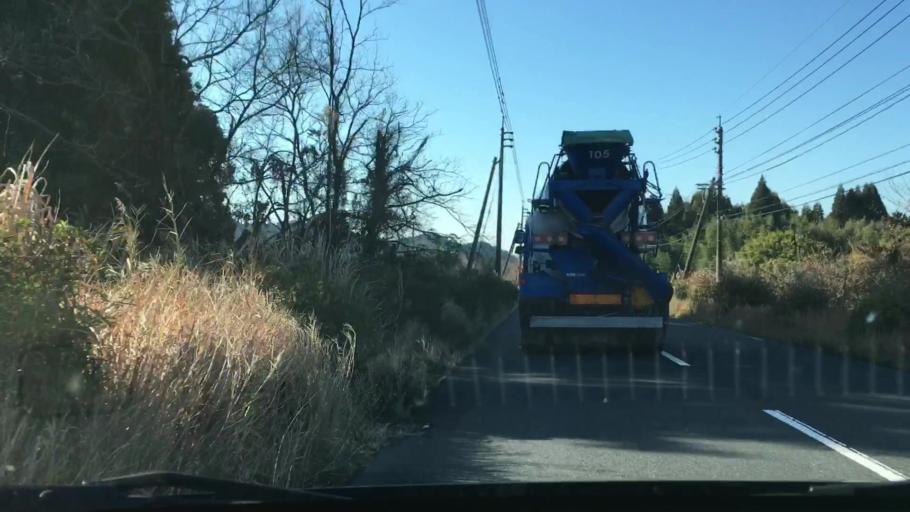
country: JP
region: Kagoshima
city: Kajiki
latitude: 31.7688
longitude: 130.6923
